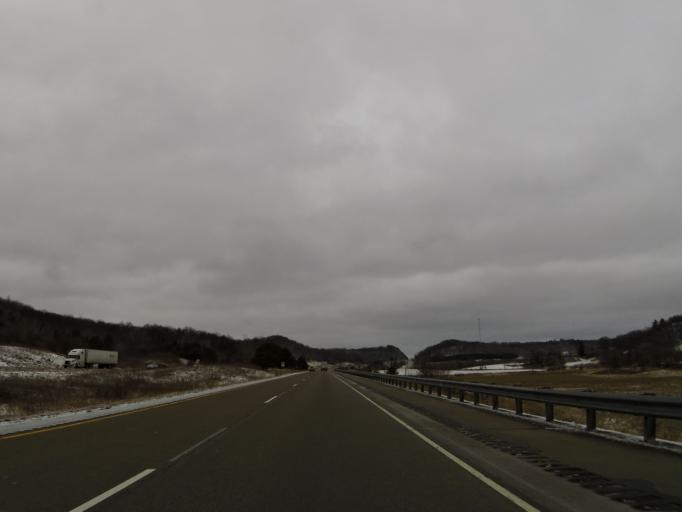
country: US
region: Wisconsin
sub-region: Trempealeau County
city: Blair
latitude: 44.4239
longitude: -91.0583
